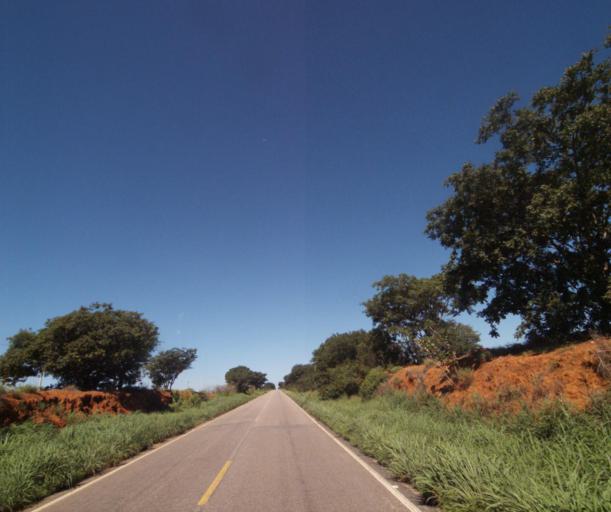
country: BR
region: Bahia
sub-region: Palmas De Monte Alto
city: Palmas de Monte Alto
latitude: -14.2604
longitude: -43.2963
